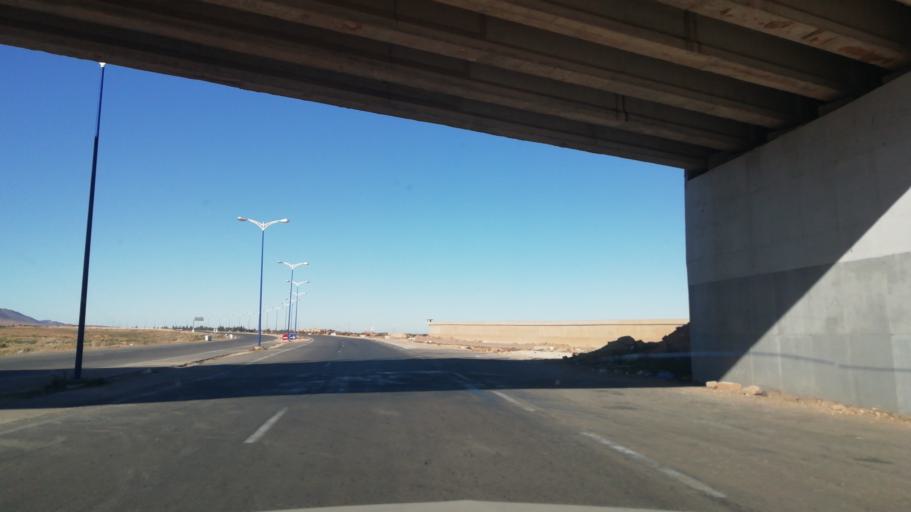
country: DZ
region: Wilaya de Naama
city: Naama
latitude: 33.5570
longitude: -0.2370
